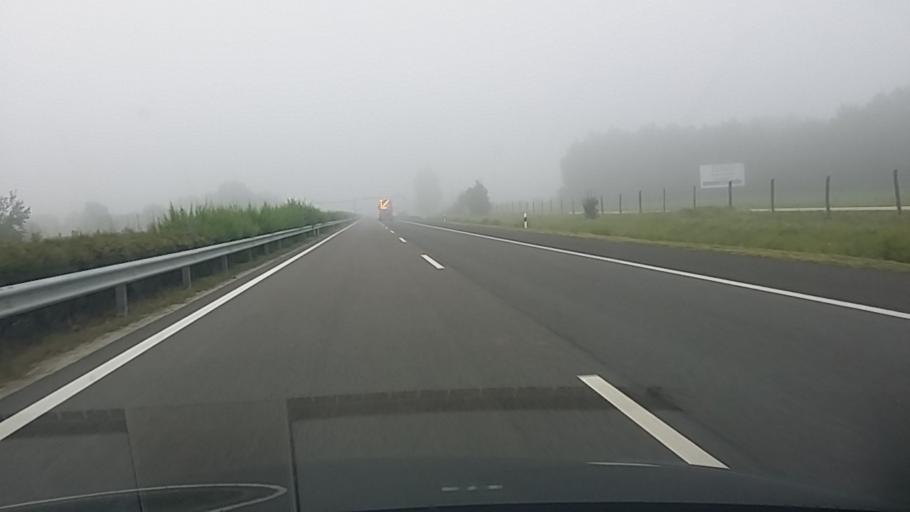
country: HU
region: Csongrad
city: Domaszek
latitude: 46.2565
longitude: 20.0380
